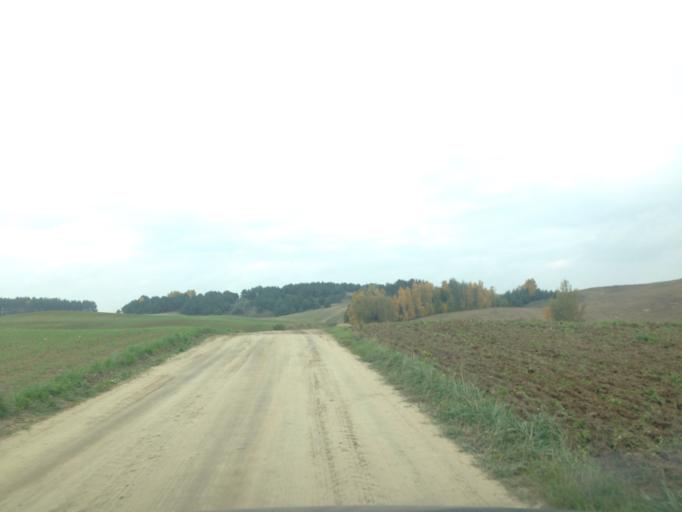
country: PL
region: Kujawsko-Pomorskie
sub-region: Powiat brodnicki
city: Brzozie
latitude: 53.3021
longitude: 19.6699
